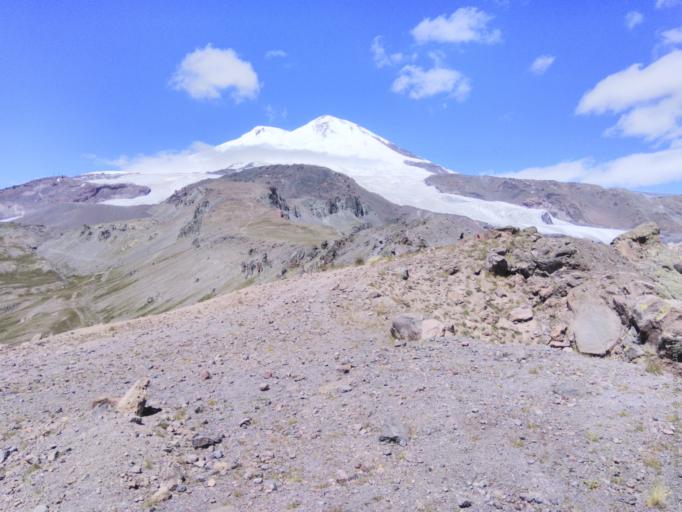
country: RU
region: Kabardino-Balkariya
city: Terskol
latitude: 43.2781
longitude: 42.4998
